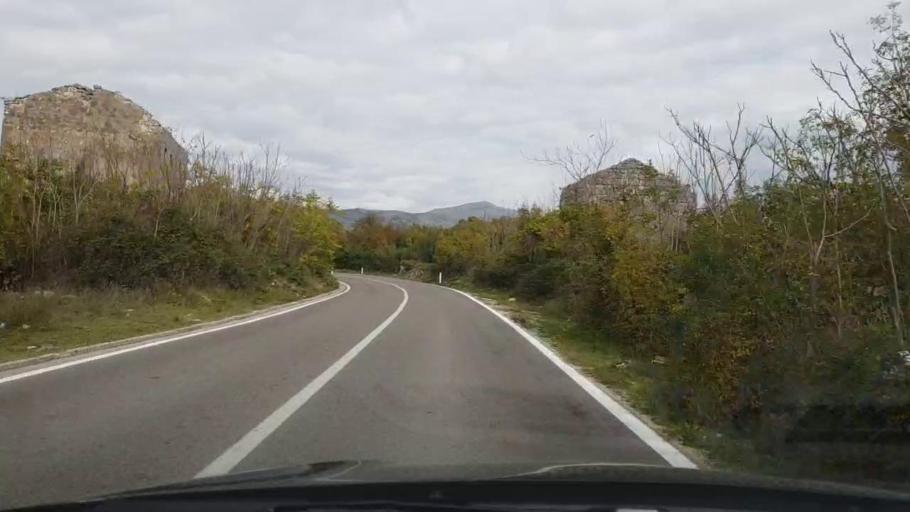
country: HR
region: Dubrovacko-Neretvanska
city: Cibaca
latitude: 42.6800
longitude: 18.2444
